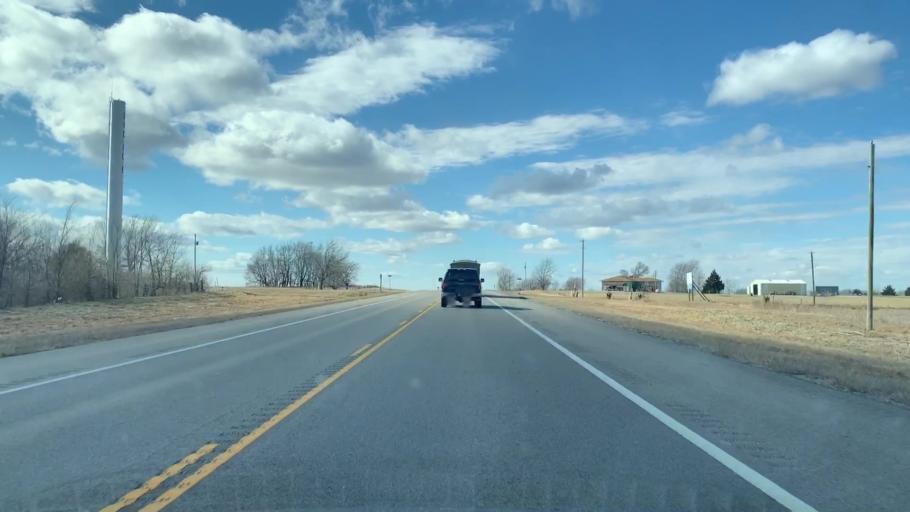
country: US
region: Kansas
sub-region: Cherokee County
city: Columbus
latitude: 37.3400
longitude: -94.9036
